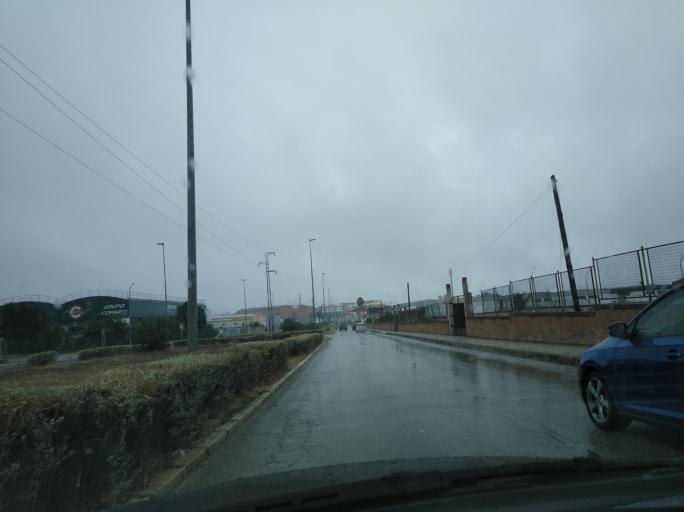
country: ES
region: Extremadura
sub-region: Provincia de Badajoz
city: Badajoz
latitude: 38.8933
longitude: -6.9924
